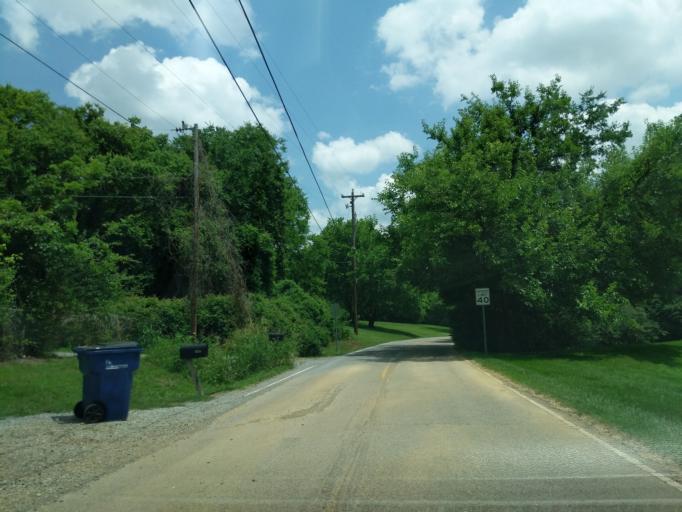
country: US
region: Tennessee
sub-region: Davidson County
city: Goodlettsville
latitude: 36.3135
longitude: -86.7345
